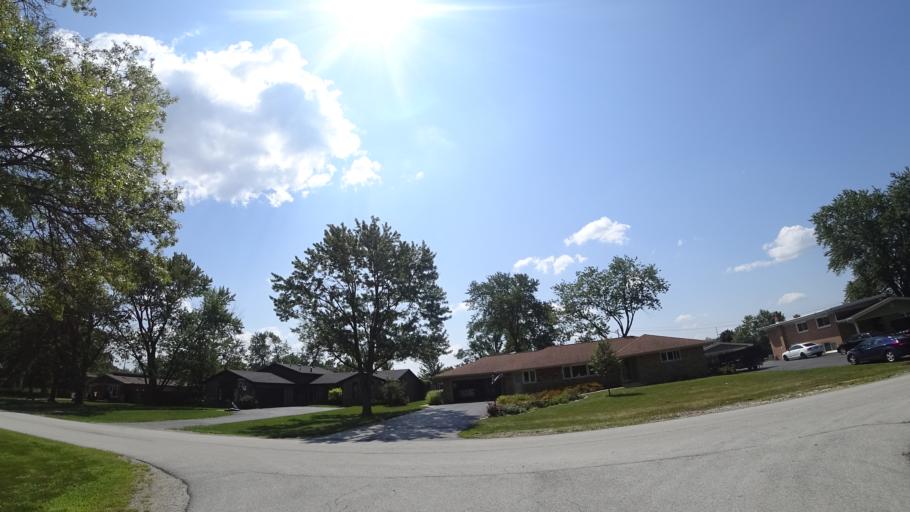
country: US
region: Illinois
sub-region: Cook County
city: Tinley Park
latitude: 41.6047
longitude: -87.7876
